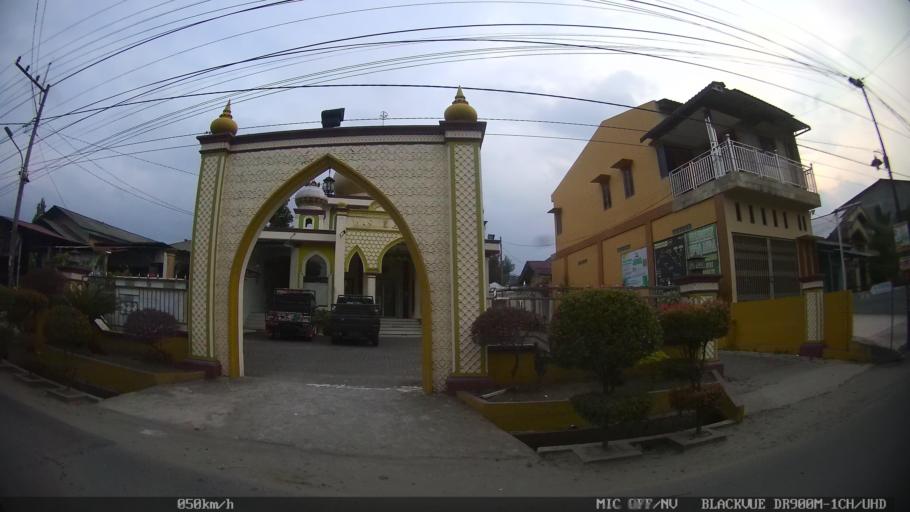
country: ID
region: North Sumatra
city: Sunggal
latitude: 3.5818
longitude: 98.6025
